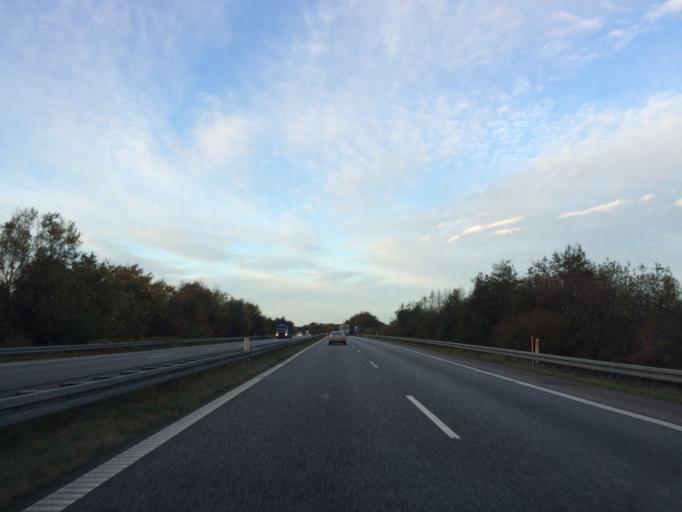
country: DK
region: South Denmark
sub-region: Haderslev Kommune
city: Vojens
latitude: 55.1629
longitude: 9.3727
